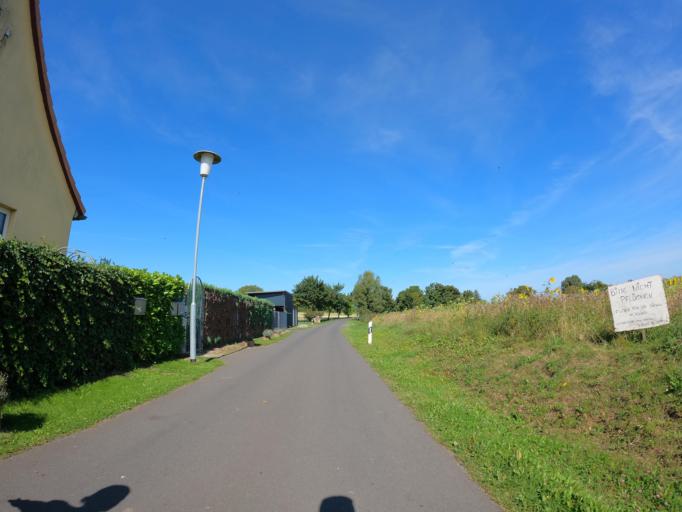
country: DE
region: Mecklenburg-Vorpommern
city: Kramerhof
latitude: 54.3775
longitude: 13.0476
